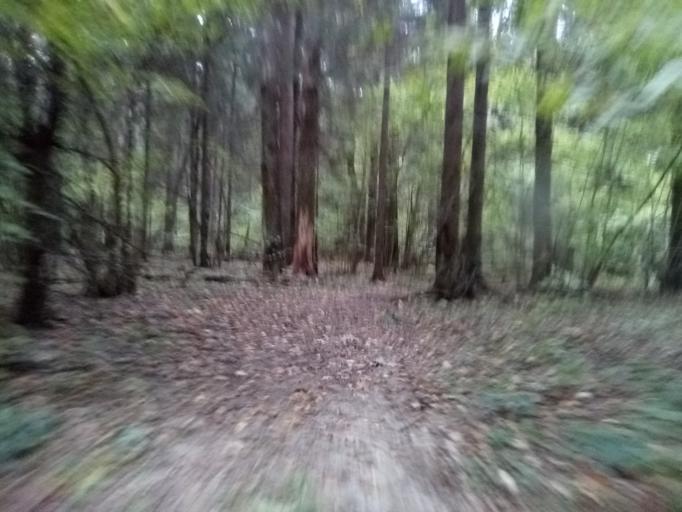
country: RU
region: Moskovskaya
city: Kokoshkino
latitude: 55.6144
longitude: 37.1891
